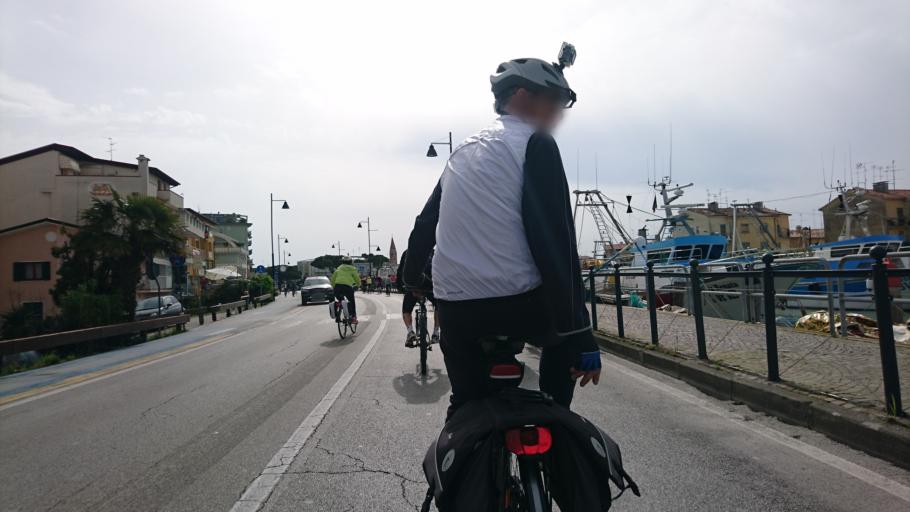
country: IT
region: Veneto
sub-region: Provincia di Venezia
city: Caorle
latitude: 45.6012
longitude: 12.8840
